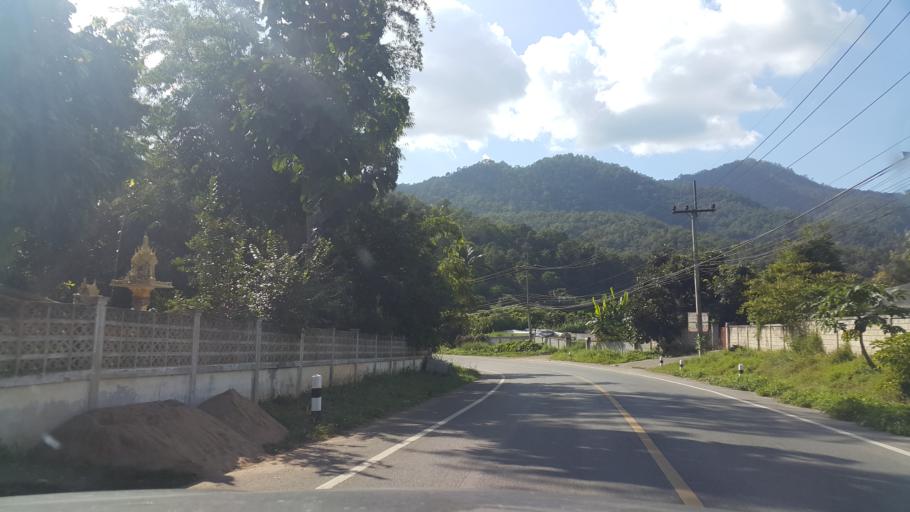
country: TH
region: Lamphun
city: Mae Tha
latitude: 18.5381
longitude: 99.2332
